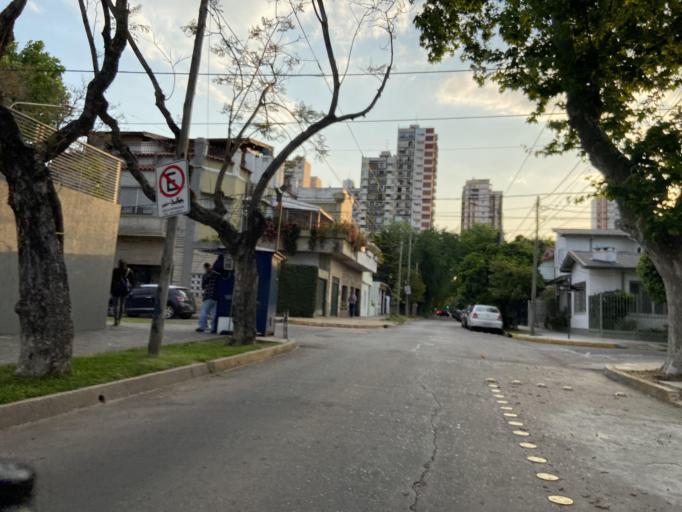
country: AR
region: Buenos Aires
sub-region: Partido de Vicente Lopez
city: Olivos
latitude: -34.5219
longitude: -58.4821
